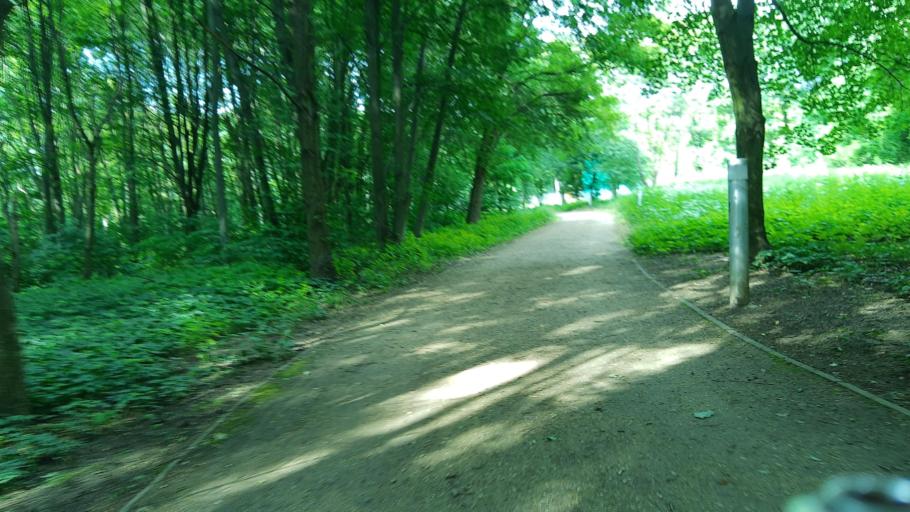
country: PL
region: Lodz Voivodeship
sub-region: Powiat sieradzki
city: Sieradz
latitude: 51.5950
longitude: 18.7548
